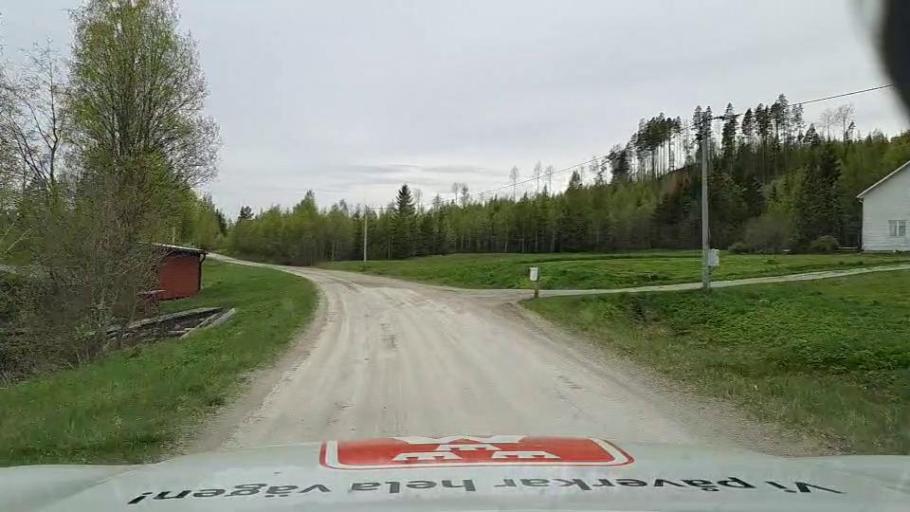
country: SE
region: Jaemtland
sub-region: Bergs Kommun
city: Hoverberg
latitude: 62.6801
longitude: 14.7693
